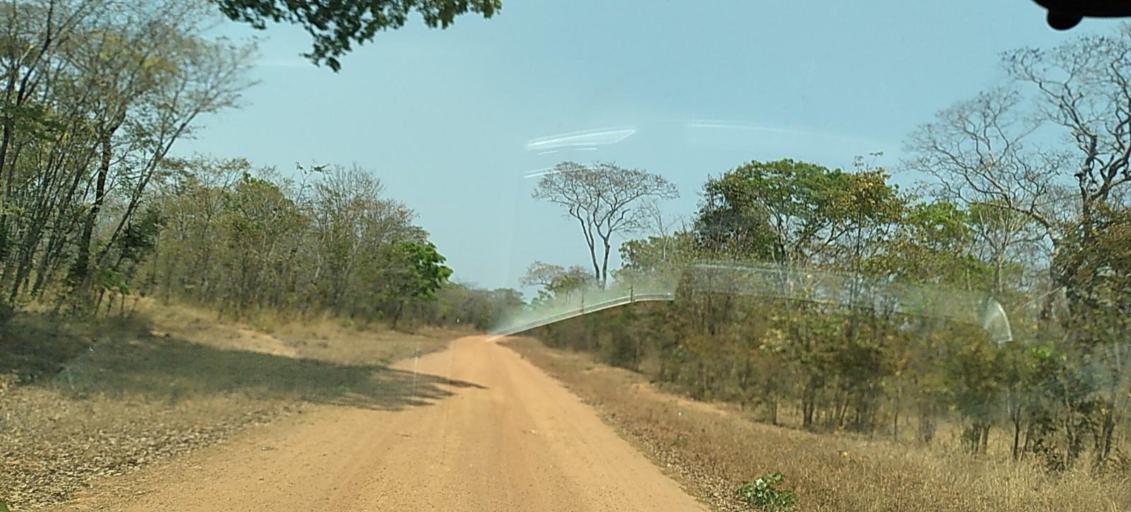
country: ZM
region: Central
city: Mumbwa
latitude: -14.3700
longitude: 26.4797
